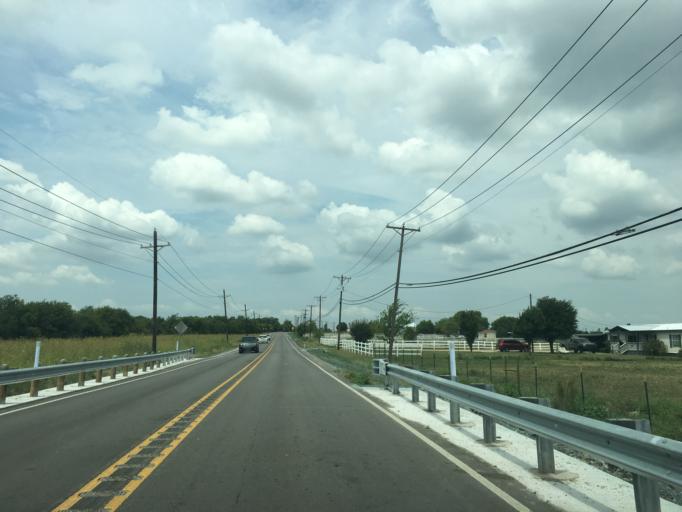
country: US
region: Texas
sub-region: Rockwall County
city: Royse City
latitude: 32.9679
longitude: -96.3617
